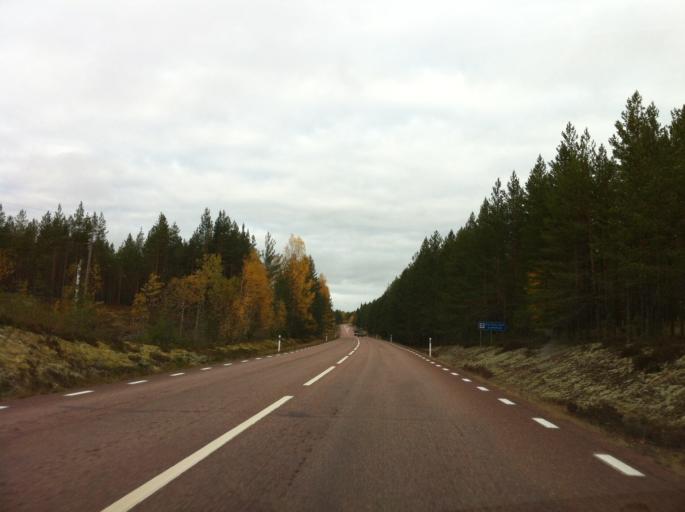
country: SE
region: Dalarna
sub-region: Mora Kommun
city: Mora
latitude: 61.0841
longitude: 14.3262
